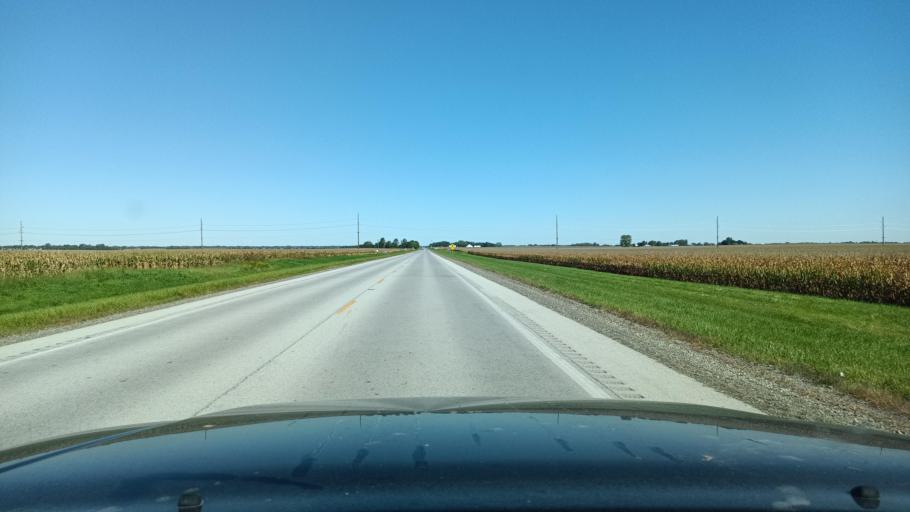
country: US
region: Illinois
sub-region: Champaign County
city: Philo
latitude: 40.0510
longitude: -88.1616
